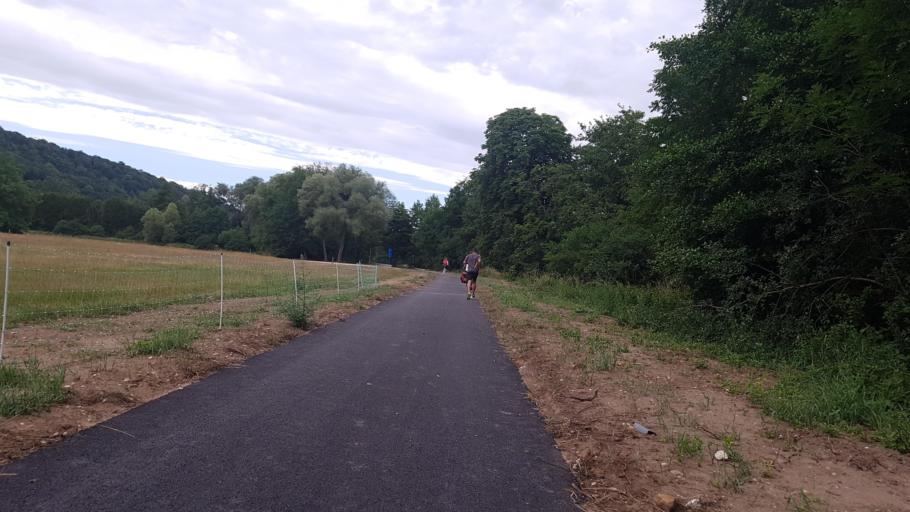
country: FR
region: Lorraine
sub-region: Departement de Meurthe-et-Moselle
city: Chaligny
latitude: 48.6309
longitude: 6.0453
